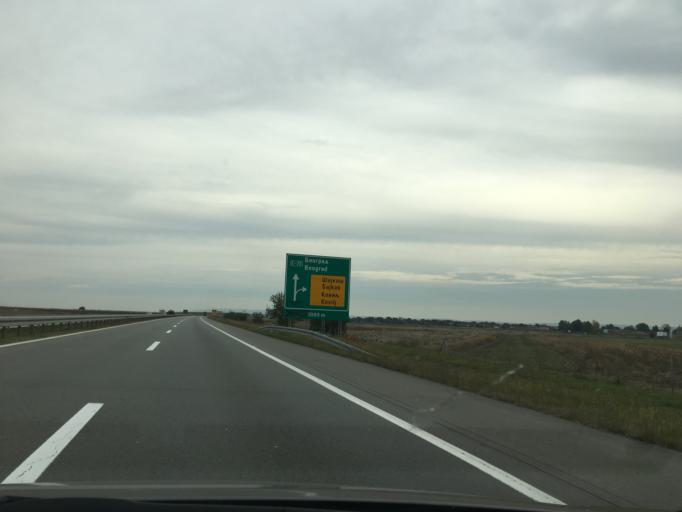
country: RS
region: Autonomna Pokrajina Vojvodina
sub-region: Juznobacki Okrug
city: Kovilj
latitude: 45.2504
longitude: 20.0198
